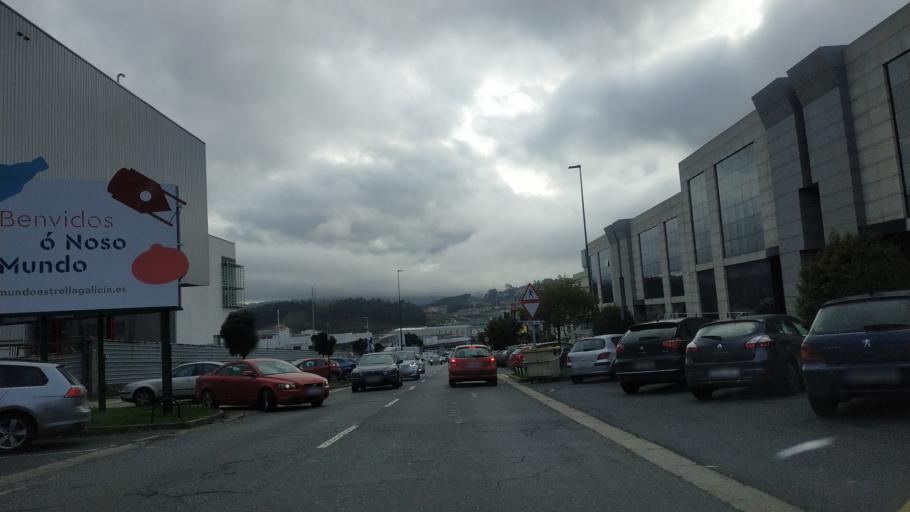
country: ES
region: Galicia
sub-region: Provincia da Coruna
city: A Coruna
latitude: 43.3537
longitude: -8.4220
